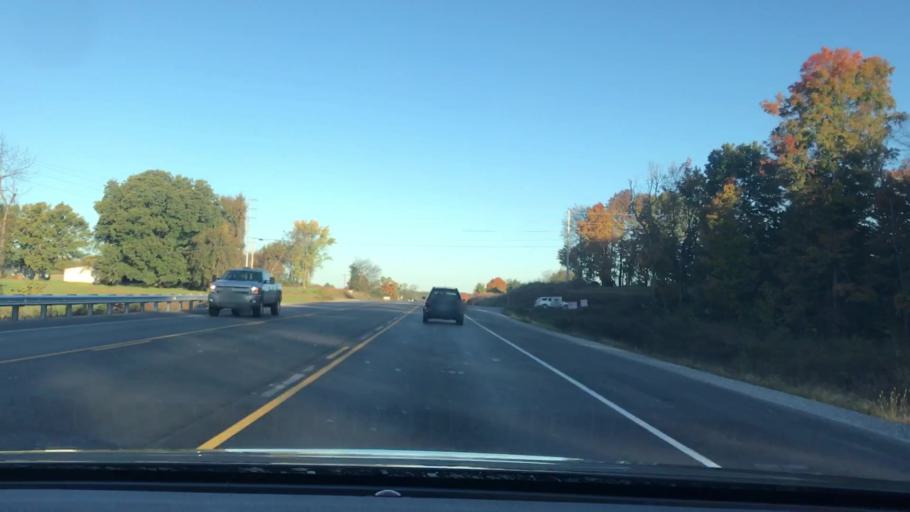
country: US
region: Kentucky
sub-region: Simpson County
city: Franklin
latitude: 36.6751
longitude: -86.5610
